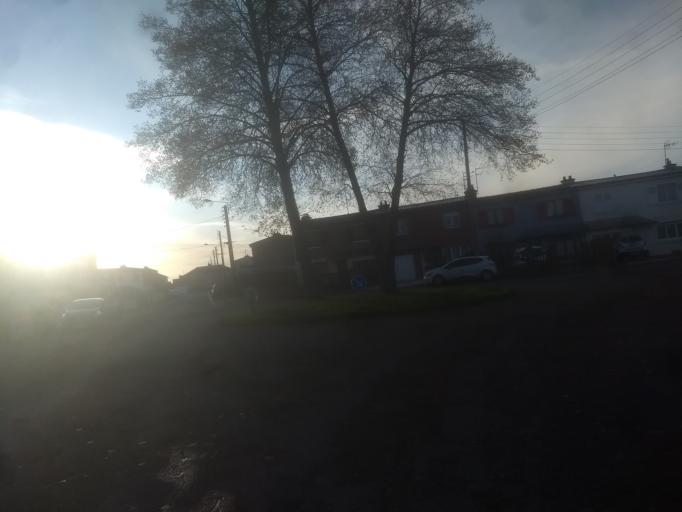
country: FR
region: Nord-Pas-de-Calais
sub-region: Departement du Pas-de-Calais
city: Beaurains
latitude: 50.2687
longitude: 2.7903
